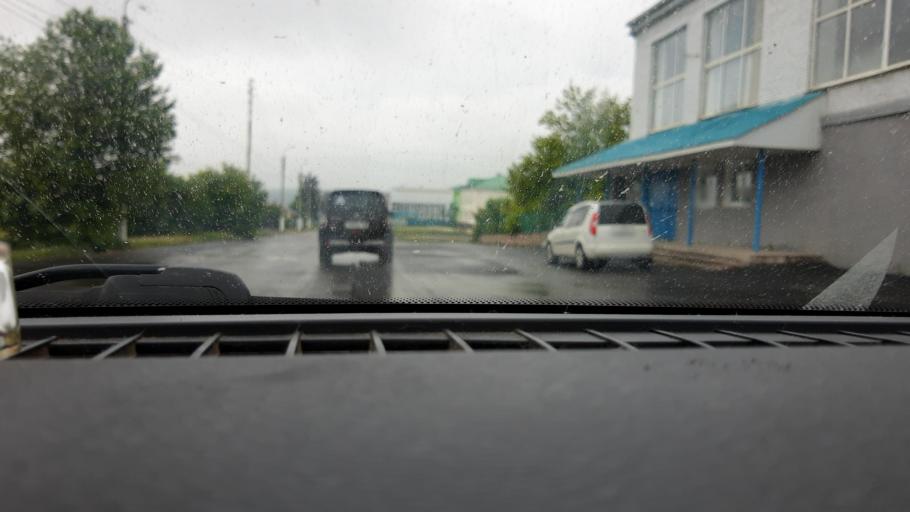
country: RU
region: Bashkortostan
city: Belebey
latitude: 54.1109
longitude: 54.1028
